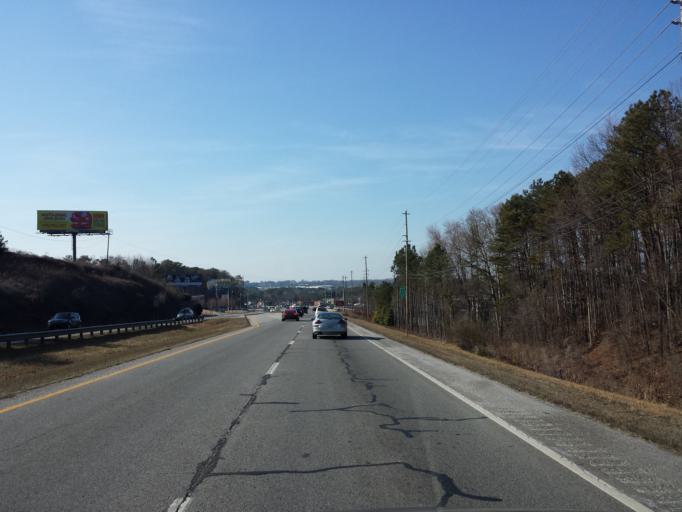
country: US
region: Georgia
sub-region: Cobb County
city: Kennesaw
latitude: 33.9958
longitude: -84.5837
